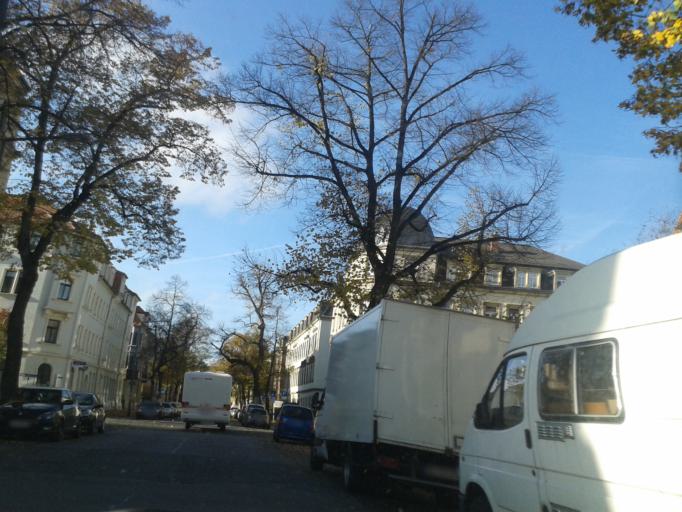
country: DE
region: Saxony
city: Albertstadt
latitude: 51.0895
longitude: 13.7268
